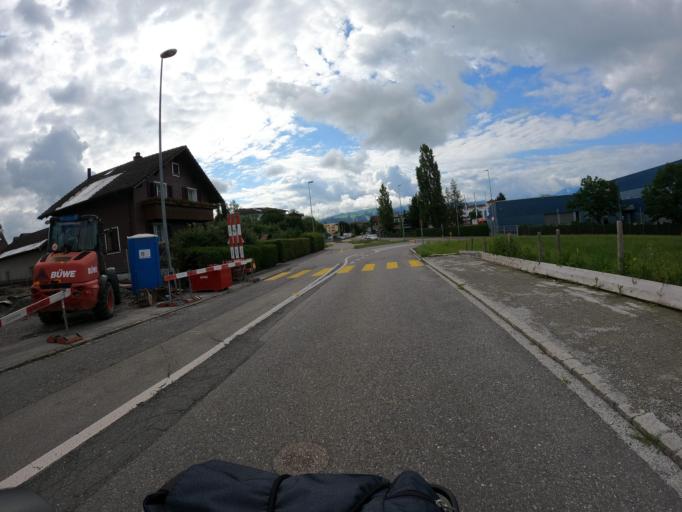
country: CH
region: Zug
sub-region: Zug
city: Steinhausen
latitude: 47.1980
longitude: 8.4787
